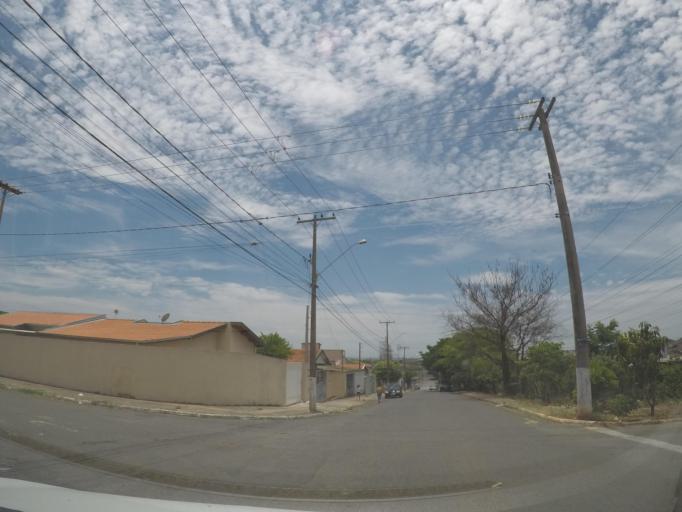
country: BR
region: Sao Paulo
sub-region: Hortolandia
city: Hortolandia
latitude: -22.8449
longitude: -47.1956
